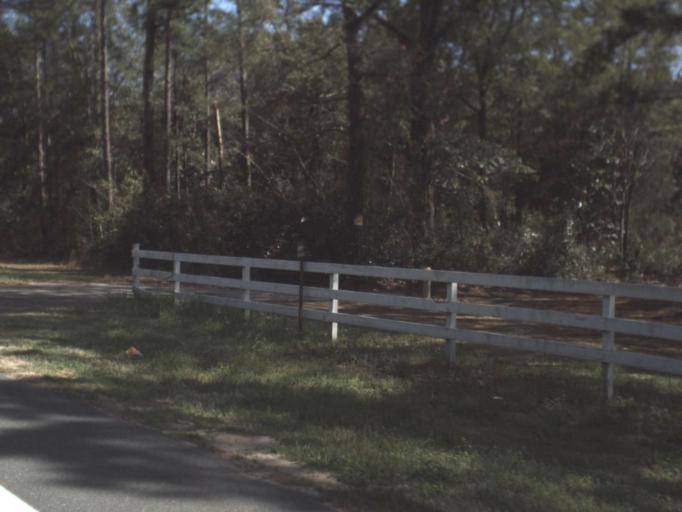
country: US
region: Florida
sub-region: Gadsden County
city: Chattahoochee
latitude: 30.6926
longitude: -84.7419
